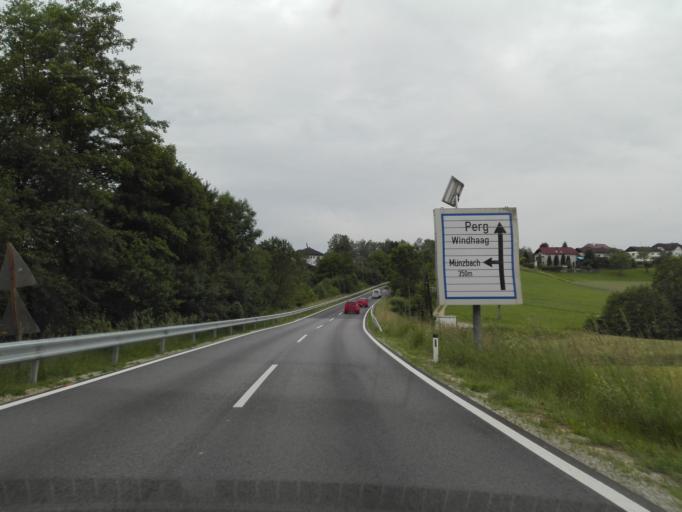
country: AT
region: Upper Austria
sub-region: Politischer Bezirk Perg
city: Perg
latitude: 48.2700
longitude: 14.7110
